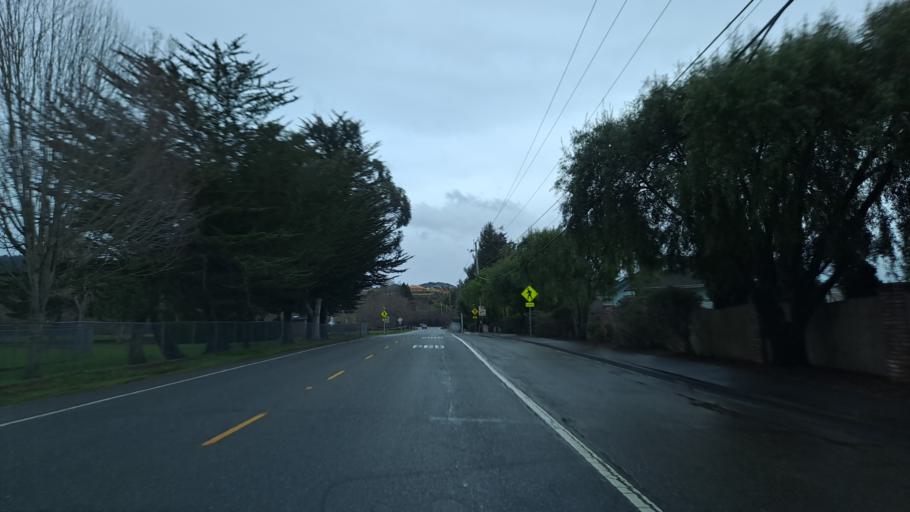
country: US
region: California
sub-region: Humboldt County
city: Fortuna
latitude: 40.5911
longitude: -124.1369
